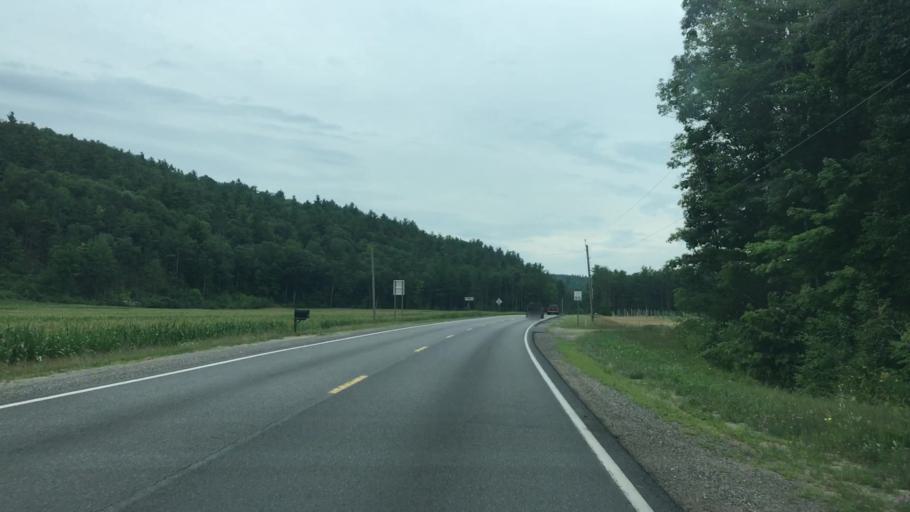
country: US
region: New York
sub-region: Clinton County
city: Peru
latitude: 44.5134
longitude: -73.5816
